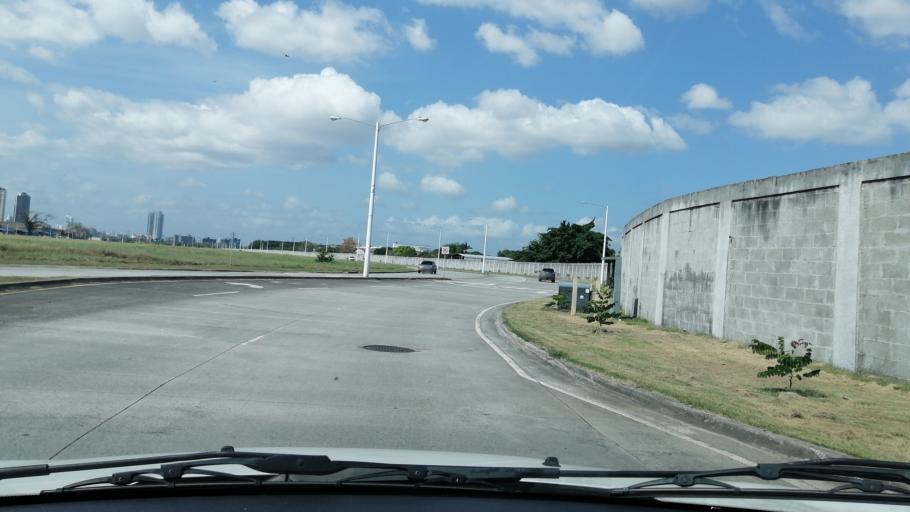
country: PA
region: Panama
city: San Miguelito
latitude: 9.0382
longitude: -79.4352
